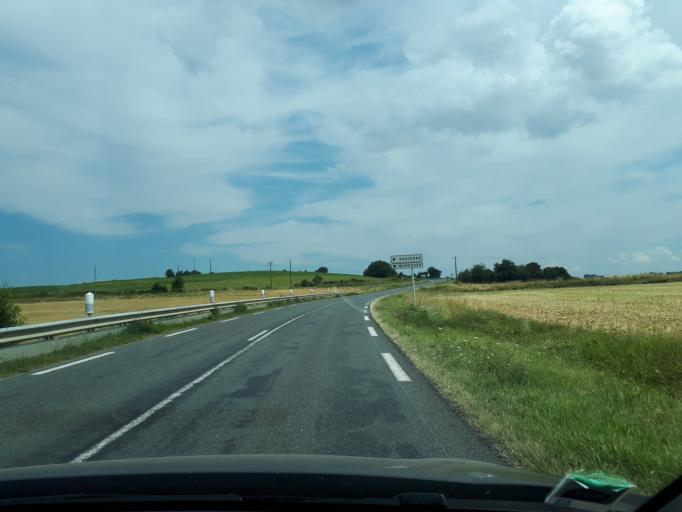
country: FR
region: Centre
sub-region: Departement du Cher
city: Rians
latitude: 47.2334
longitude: 2.6431
